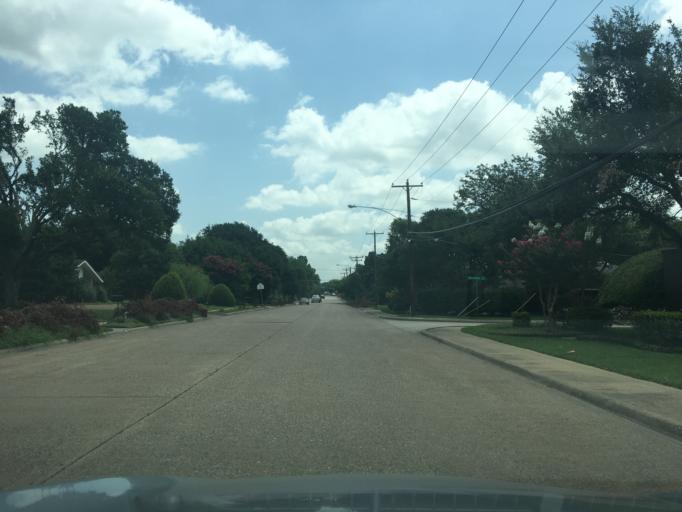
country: US
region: Texas
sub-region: Dallas County
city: Addison
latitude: 32.9144
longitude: -96.8227
